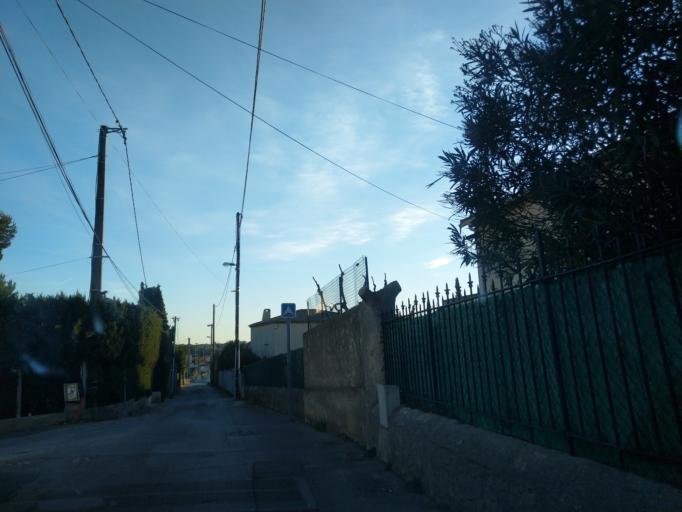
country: FR
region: Provence-Alpes-Cote d'Azur
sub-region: Departement des Bouches-du-Rhone
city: Plan-de-Cuques
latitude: 43.3402
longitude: 5.4506
